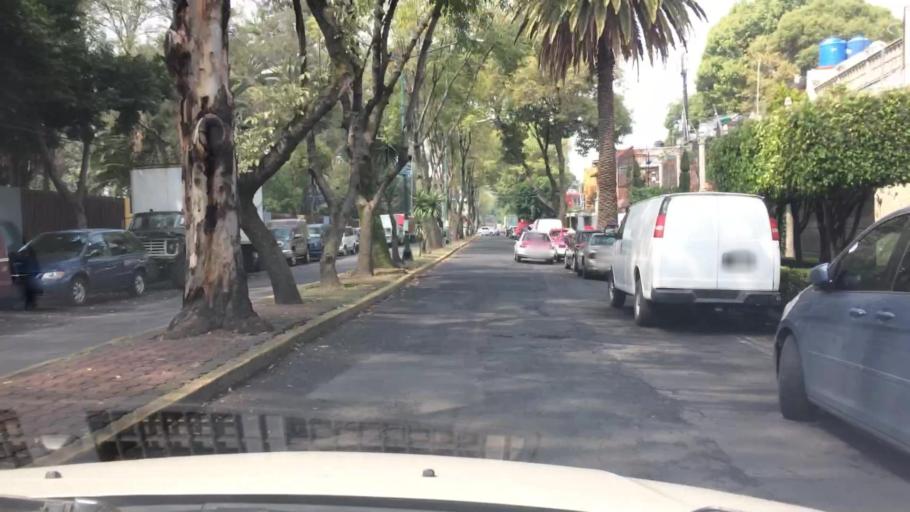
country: MX
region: Mexico City
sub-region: Iztacalco
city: Iztacalco
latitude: 19.4116
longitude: -99.1074
